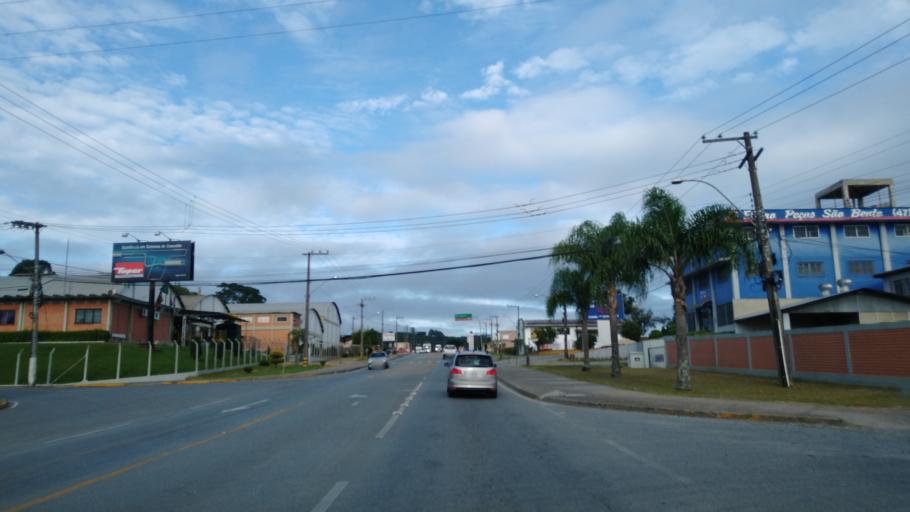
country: BR
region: Santa Catarina
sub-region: Sao Bento Do Sul
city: Sao Bento do Sul
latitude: -26.2243
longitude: -49.4096
